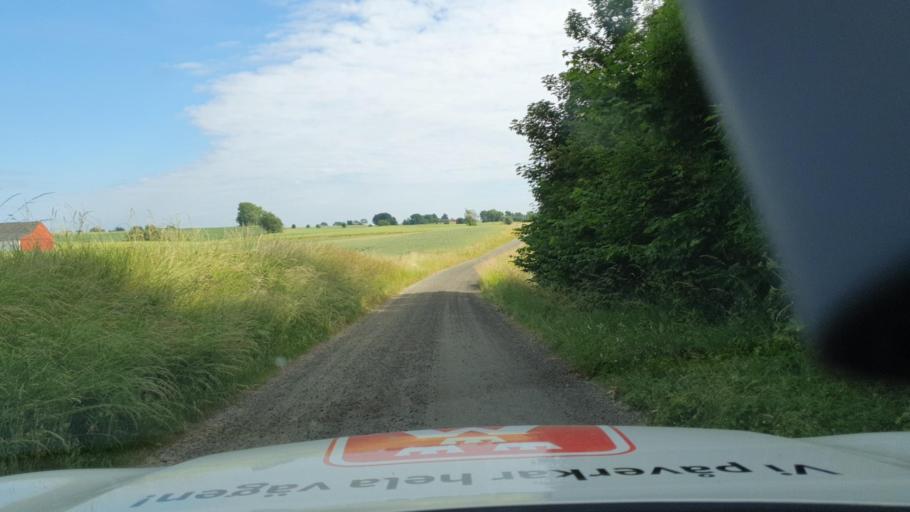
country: SE
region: Skane
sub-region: Skurups Kommun
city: Rydsgard
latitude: 55.4481
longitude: 13.5940
